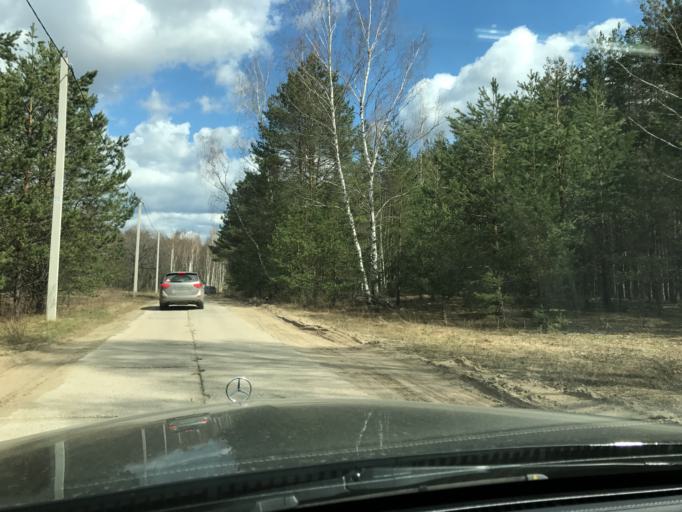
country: RU
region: Vladimir
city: Pokrov
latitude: 55.8591
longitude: 39.2040
